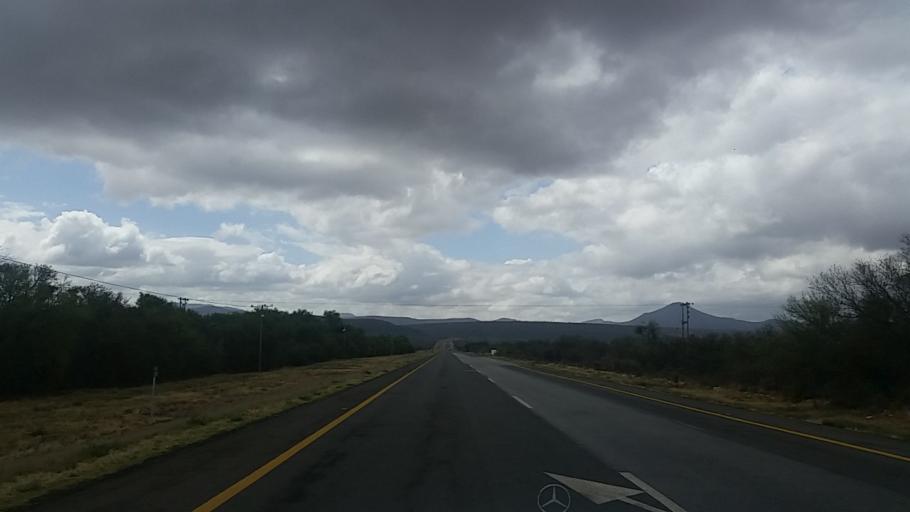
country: ZA
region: Eastern Cape
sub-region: Cacadu District Municipality
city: Graaff-Reinet
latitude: -32.1759
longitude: 24.5651
